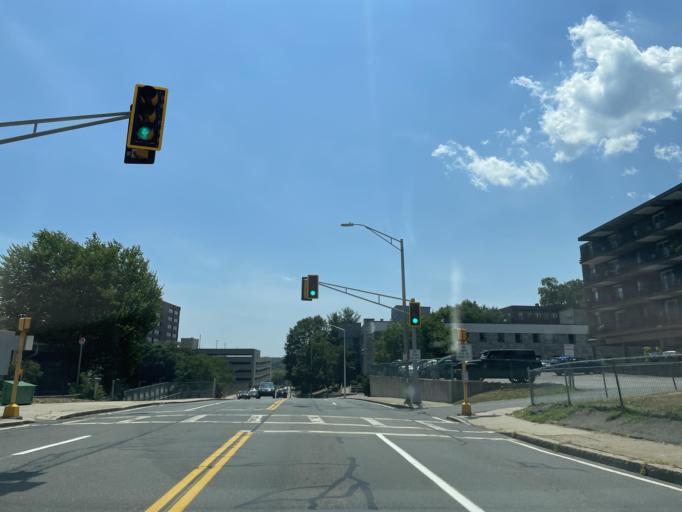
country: US
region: Massachusetts
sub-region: Norfolk County
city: Quincy
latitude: 42.2515
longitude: -71.0057
